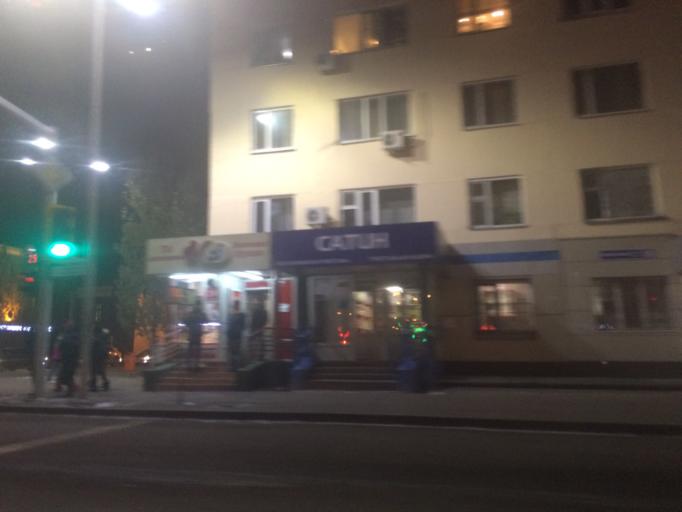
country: KZ
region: Astana Qalasy
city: Astana
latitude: 51.1858
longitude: 71.4160
